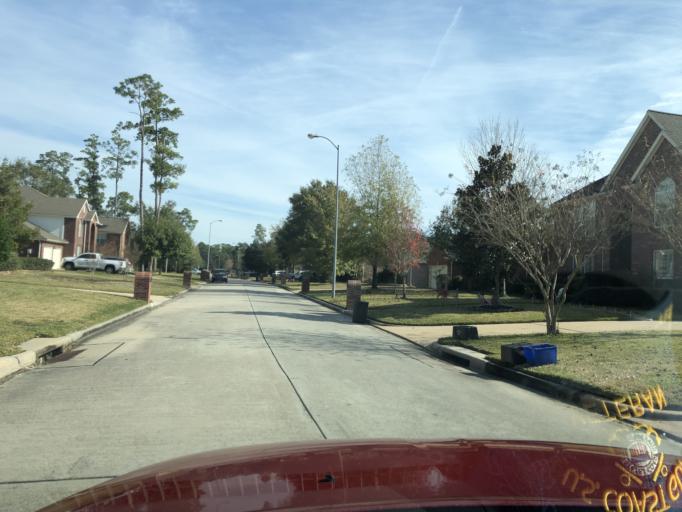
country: US
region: Texas
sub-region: Harris County
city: Tomball
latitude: 30.0249
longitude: -95.5587
